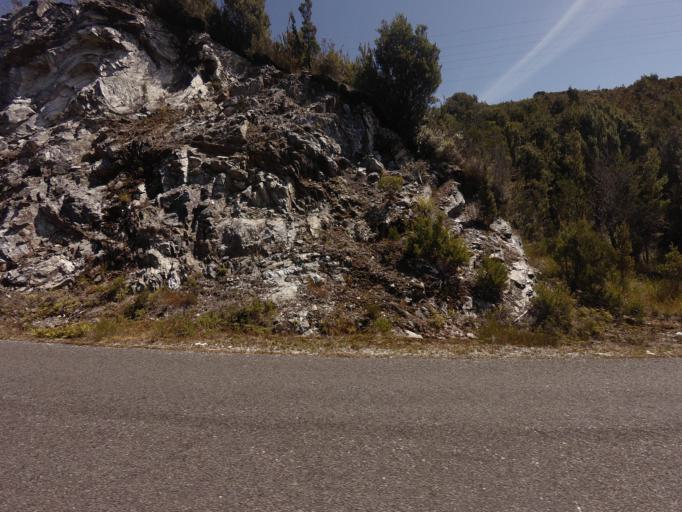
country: AU
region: Tasmania
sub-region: West Coast
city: Queenstown
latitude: -42.7465
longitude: 145.9810
